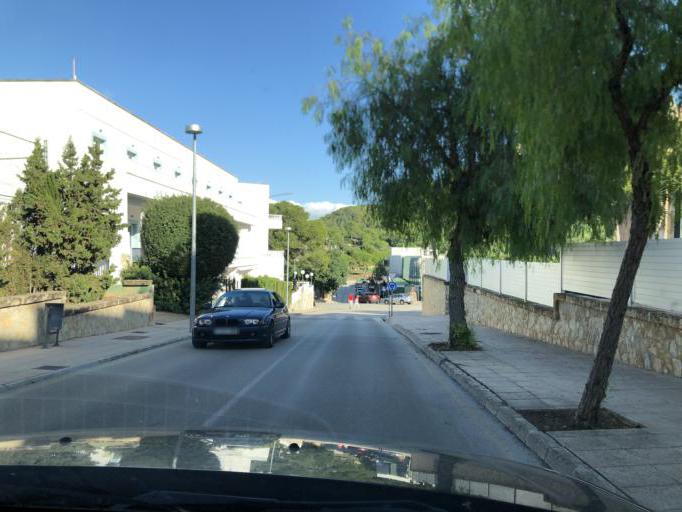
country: ES
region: Balearic Islands
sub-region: Illes Balears
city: Camp de Mar
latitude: 39.5389
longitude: 2.4215
